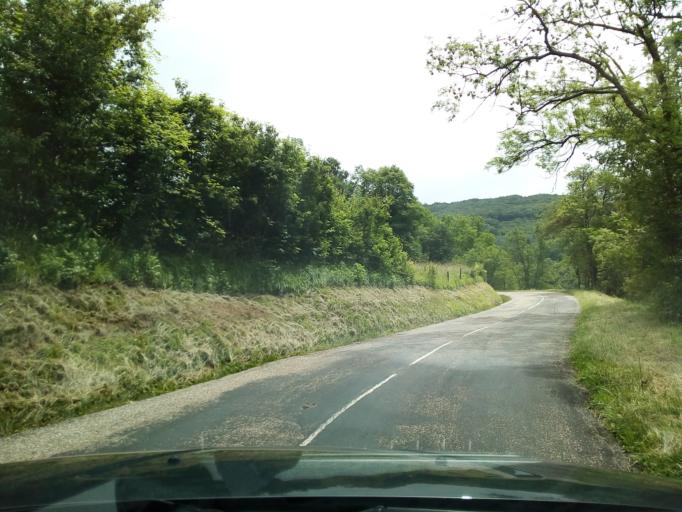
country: FR
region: Rhone-Alpes
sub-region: Departement de l'Isere
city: Saint-Martin-d'Heres
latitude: 45.1647
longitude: 5.7816
